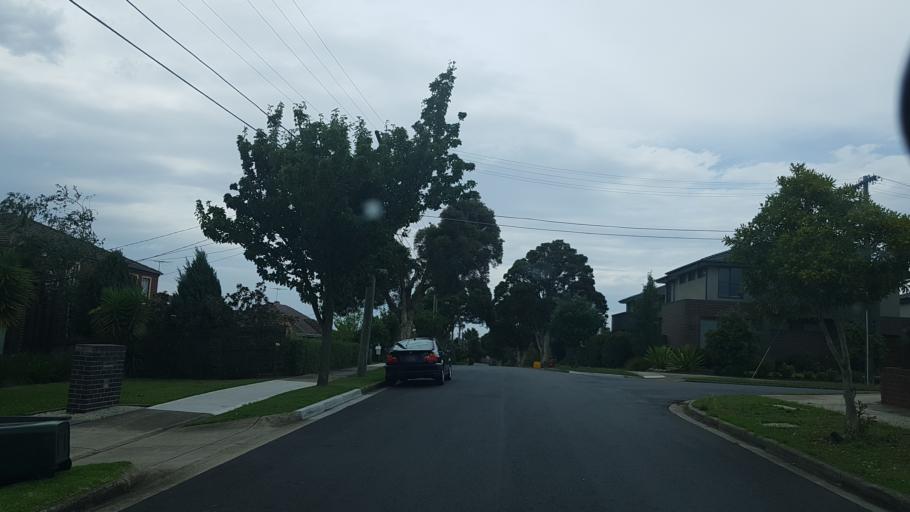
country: AU
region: Victoria
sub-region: Manningham
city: Bulleen
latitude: -37.7639
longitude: 145.0878
